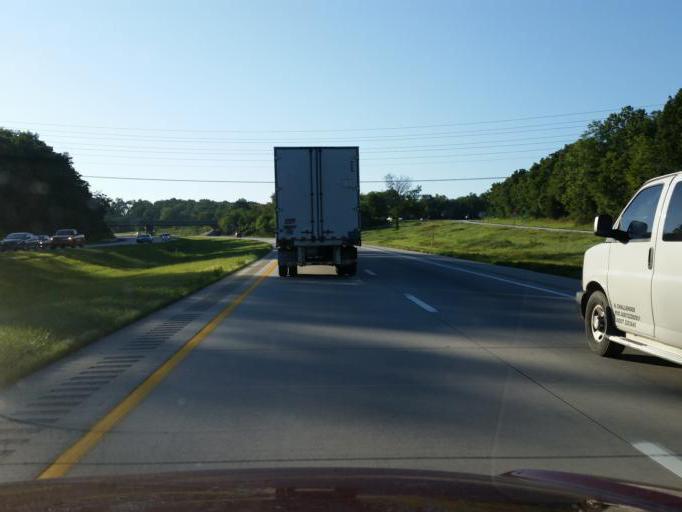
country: US
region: Pennsylvania
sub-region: Dauphin County
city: Middletown
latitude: 40.1957
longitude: -76.6900
